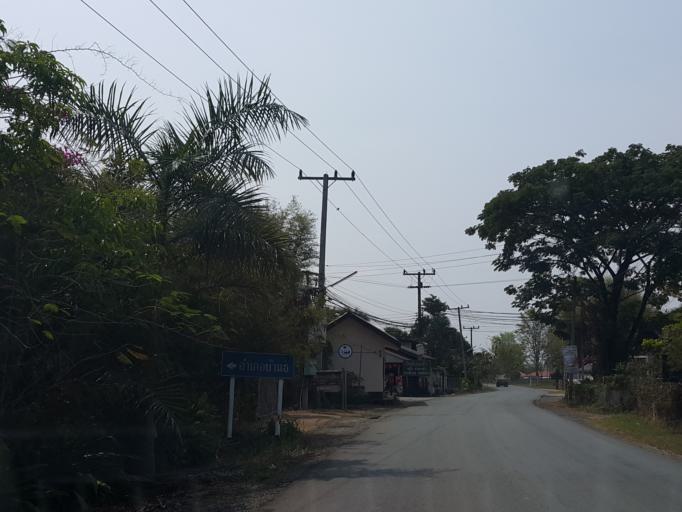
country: TH
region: Lamphun
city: Ban Thi
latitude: 18.6859
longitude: 99.1022
